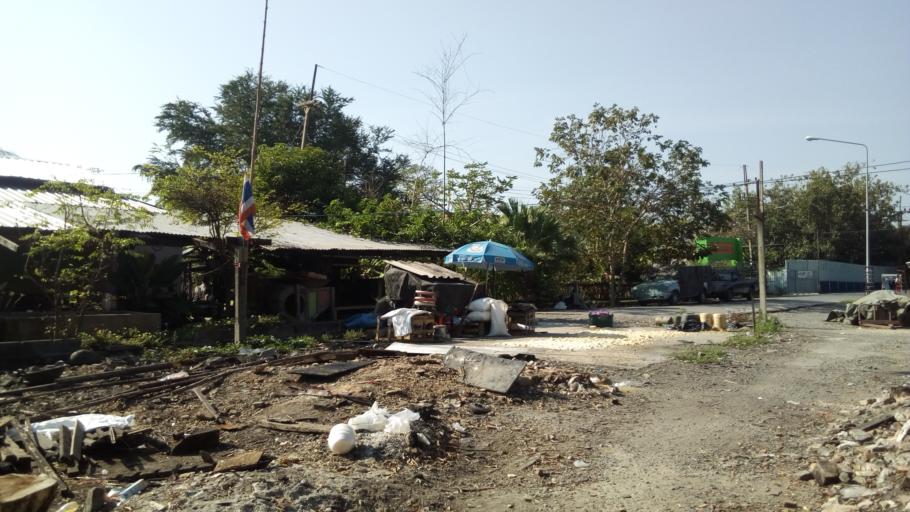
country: TH
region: Pathum Thani
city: Ban Rangsit
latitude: 14.0517
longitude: 100.8232
